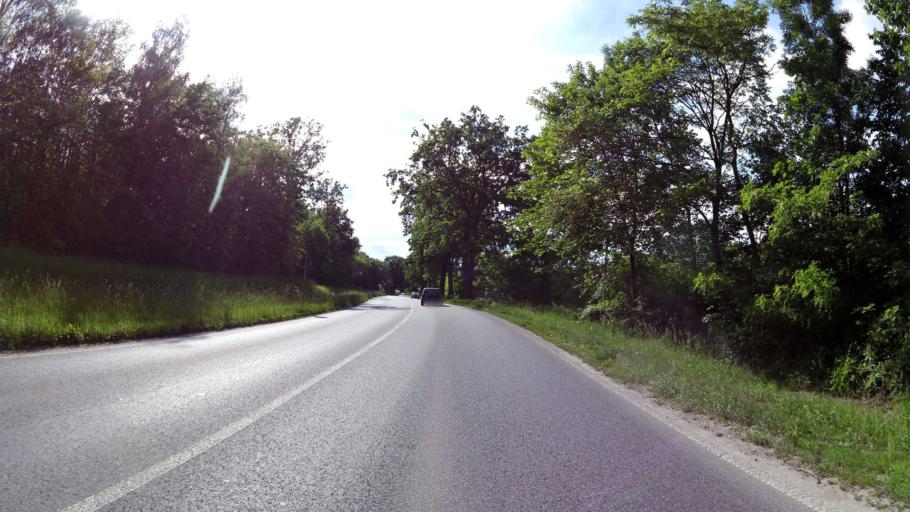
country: DE
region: Brandenburg
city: Petershagen
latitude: 52.4871
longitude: 13.8195
